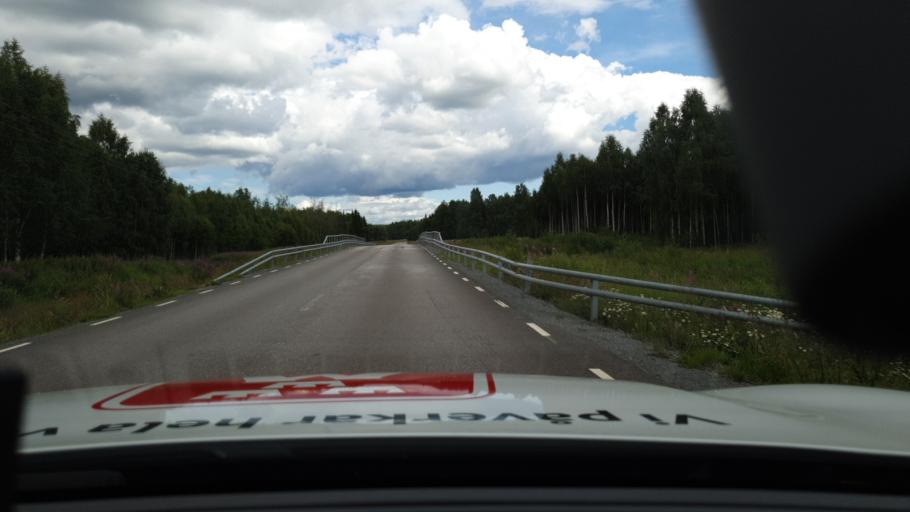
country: SE
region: Norrbotten
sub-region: Lulea Kommun
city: Sodra Sunderbyn
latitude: 65.8232
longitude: 21.9246
